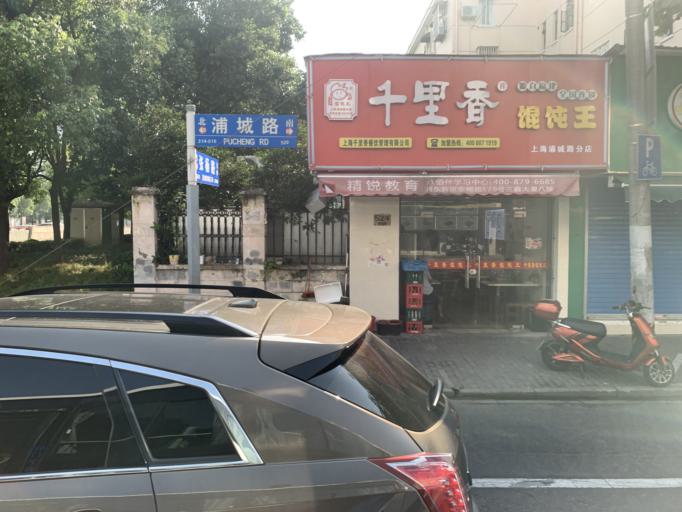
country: CN
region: Shanghai Shi
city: Pudong
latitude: 31.2278
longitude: 121.5092
